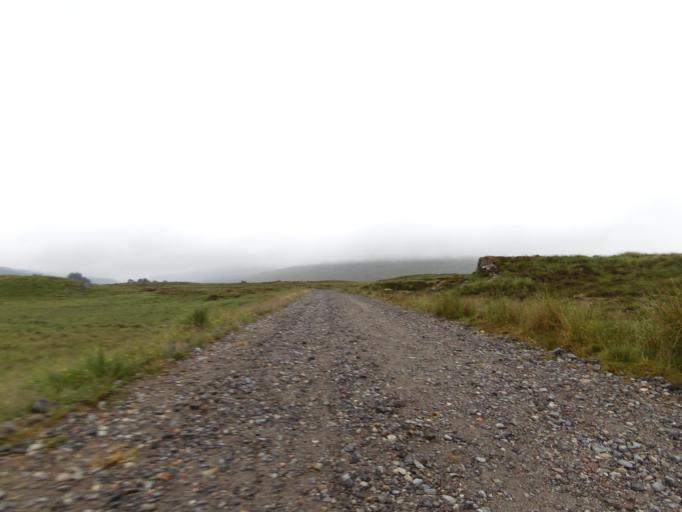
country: GB
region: Scotland
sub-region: Highland
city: Spean Bridge
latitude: 56.7640
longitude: -4.6751
